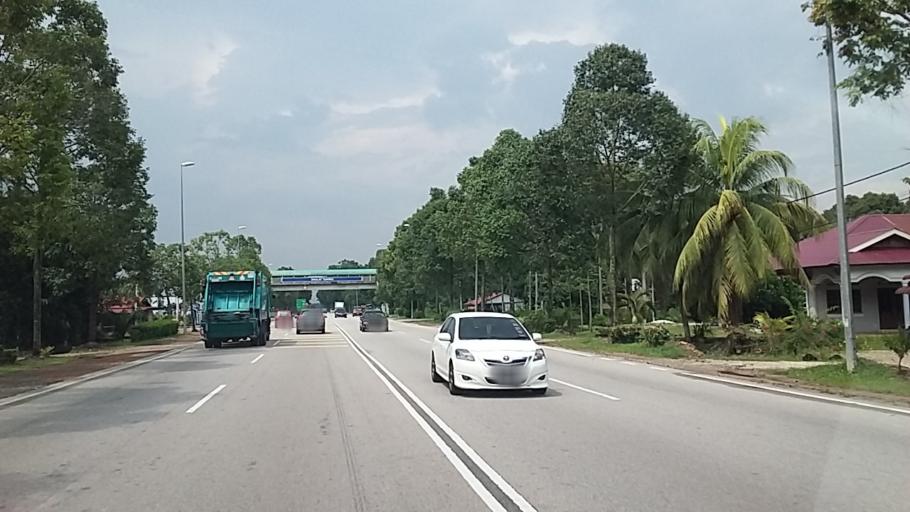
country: MY
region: Johor
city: Parit Raja
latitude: 1.8705
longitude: 103.1276
